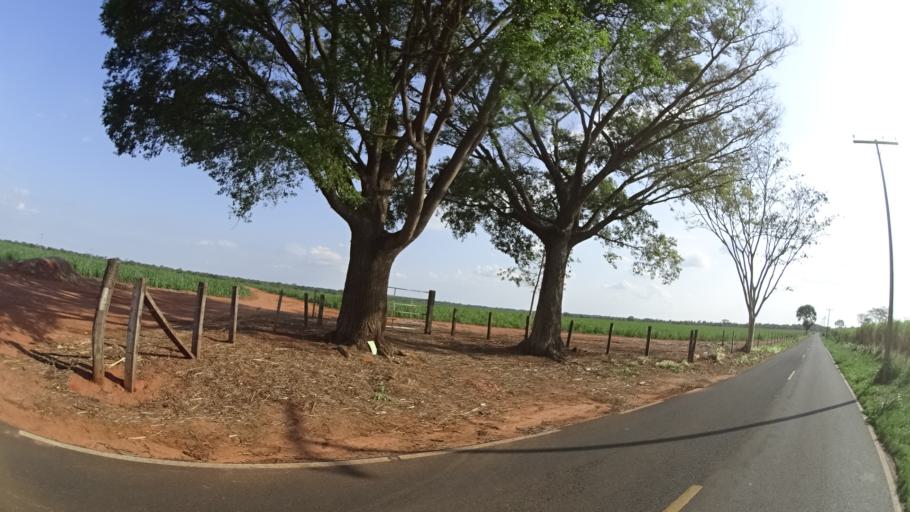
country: BR
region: Sao Paulo
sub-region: Urupes
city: Urupes
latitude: -21.3896
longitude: -49.5021
